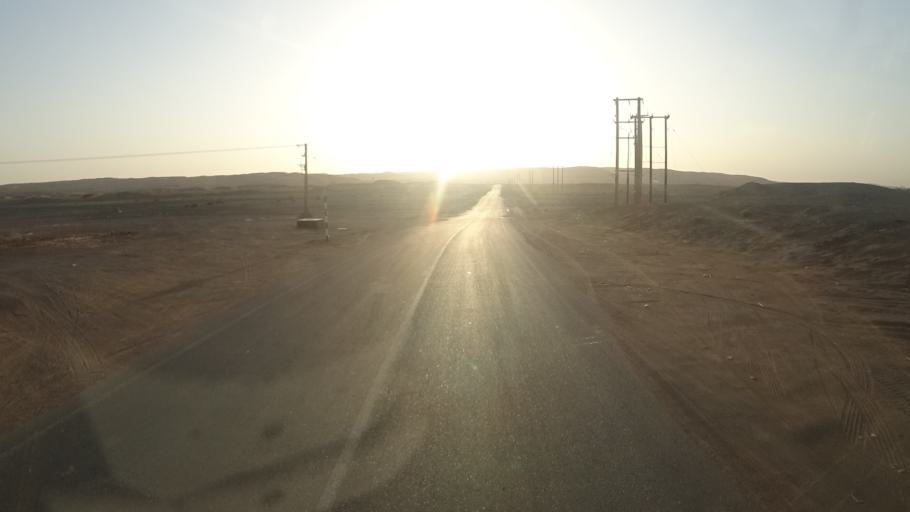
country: OM
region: Ash Sharqiyah
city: Badiyah
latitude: 22.4984
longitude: 58.7390
